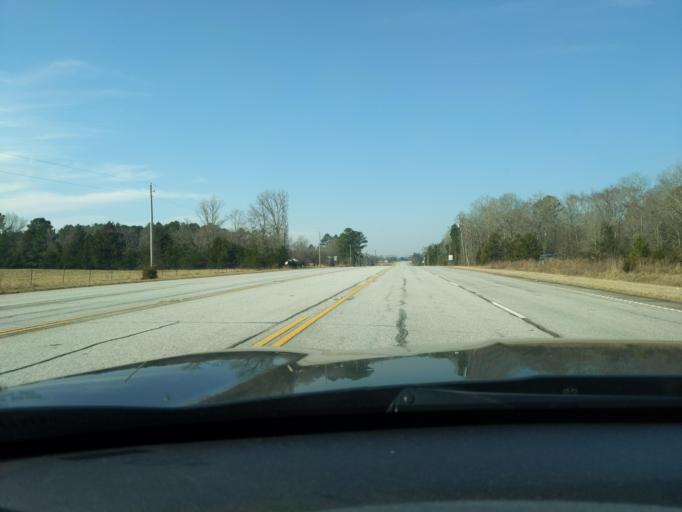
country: US
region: South Carolina
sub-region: Abbeville County
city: Calhoun Falls
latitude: 34.0984
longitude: -82.5566
